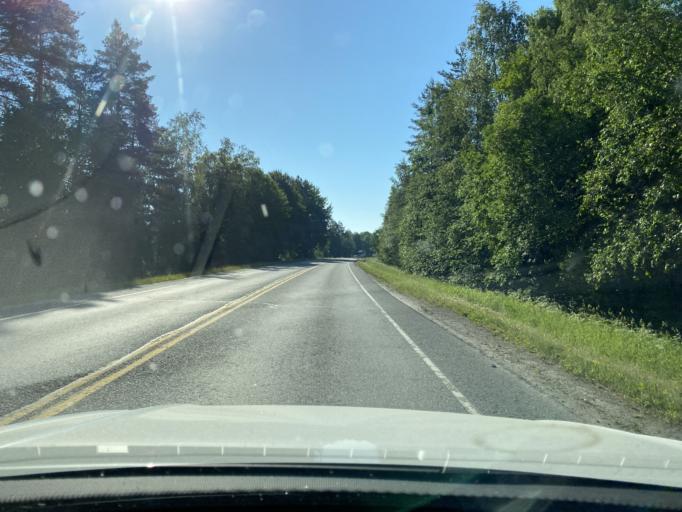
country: FI
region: Haeme
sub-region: Forssa
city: Tammela
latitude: 60.8296
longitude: 23.7271
